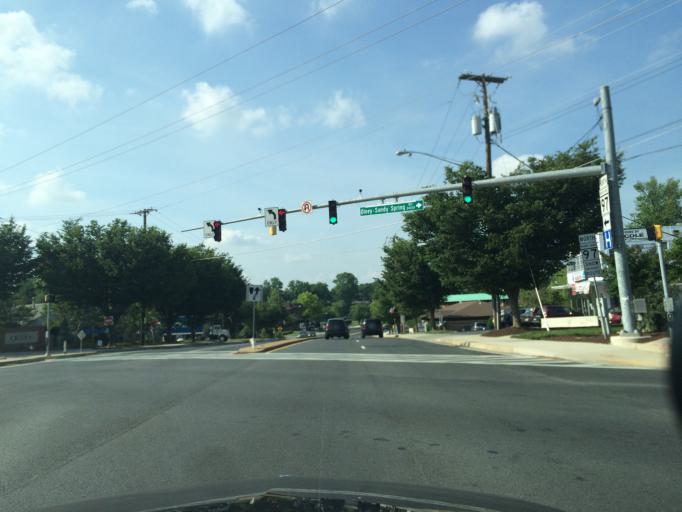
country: US
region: Maryland
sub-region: Montgomery County
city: Olney
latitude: 39.1530
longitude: -77.0668
